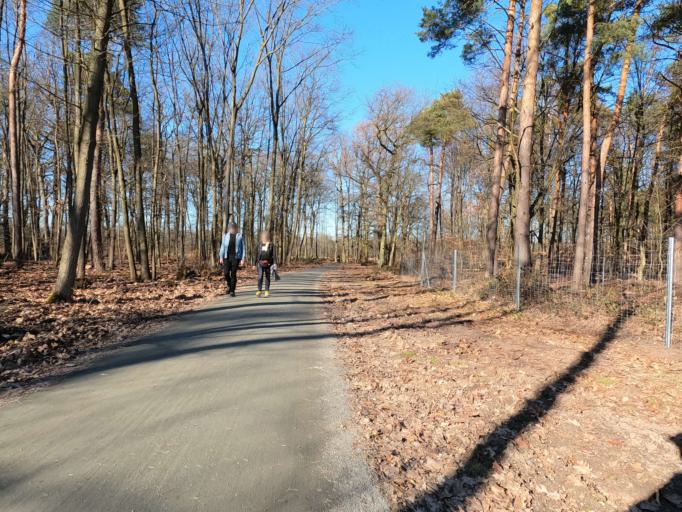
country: DE
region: Hesse
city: Kelsterbach
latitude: 50.0749
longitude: 8.5652
